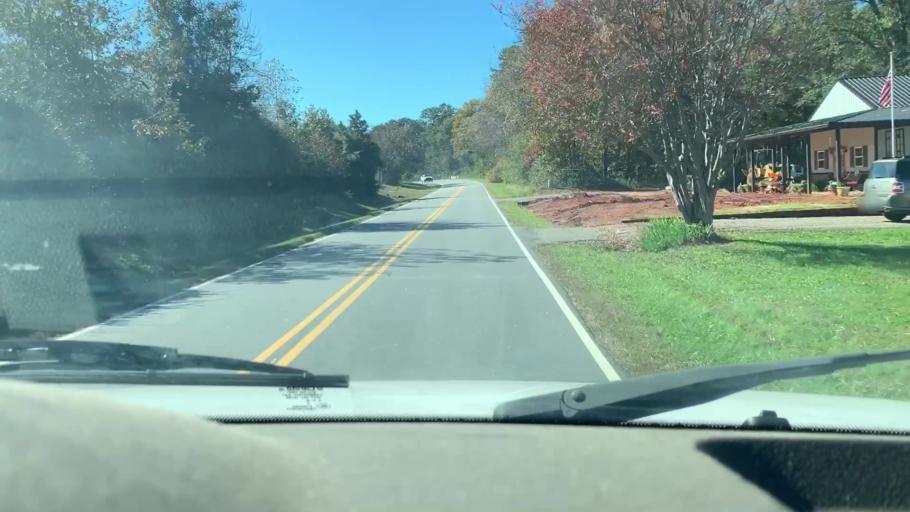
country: US
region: North Carolina
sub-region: Lincoln County
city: Westport
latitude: 35.4815
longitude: -80.9890
